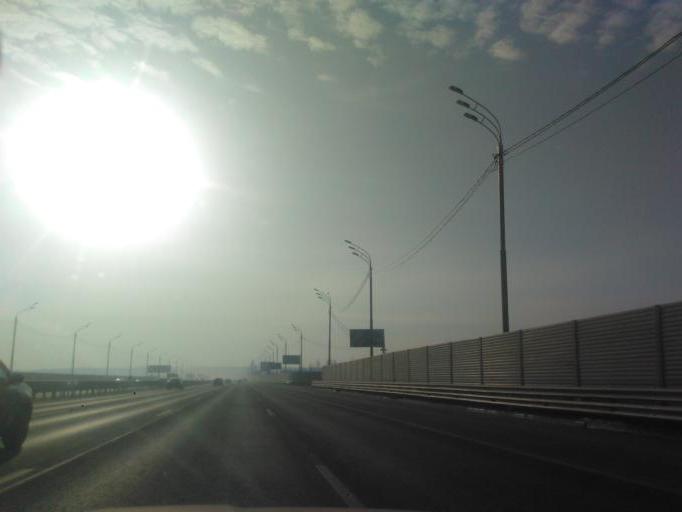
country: RU
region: Moskovskaya
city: Pavlovskaya Sloboda
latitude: 55.7964
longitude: 37.0482
